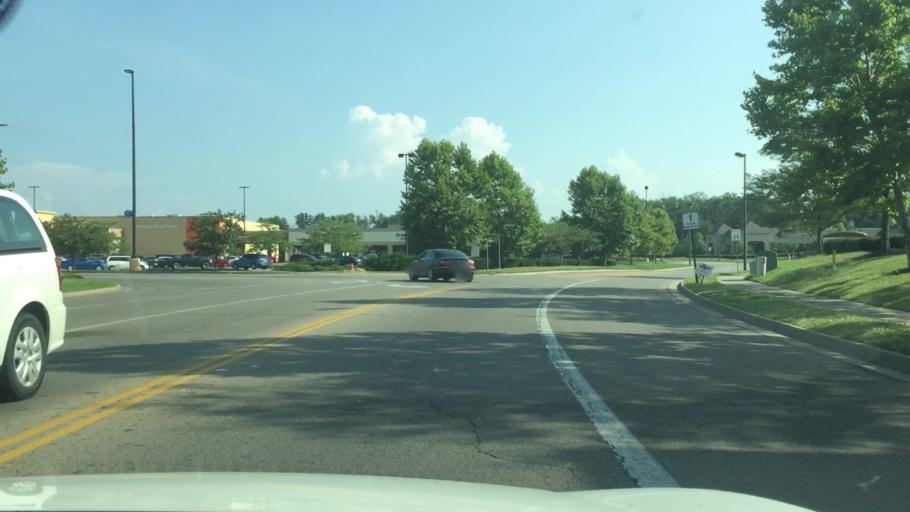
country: US
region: Ohio
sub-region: Clark County
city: Springfield
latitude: 39.9229
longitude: -83.7484
